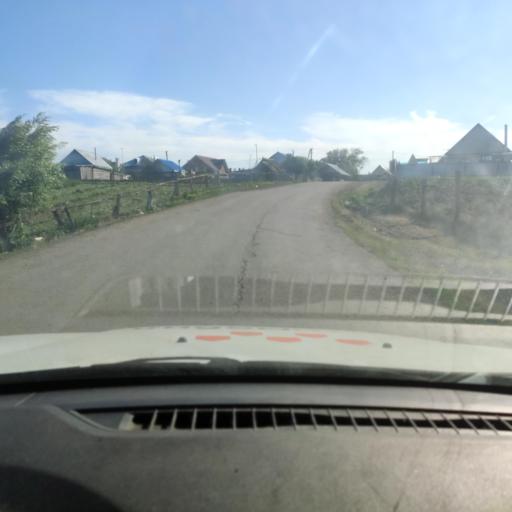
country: RU
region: Bashkortostan
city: Mikhaylovka
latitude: 54.9624
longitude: 55.7987
